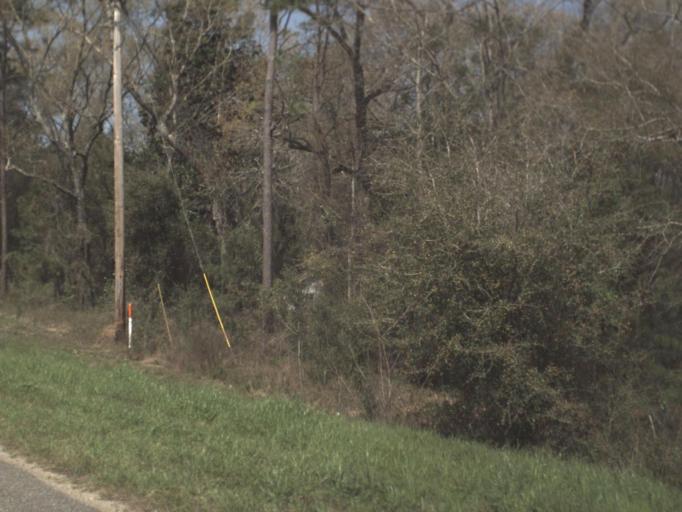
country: US
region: Florida
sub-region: Liberty County
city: Bristol
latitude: 30.4322
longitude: -84.9480
